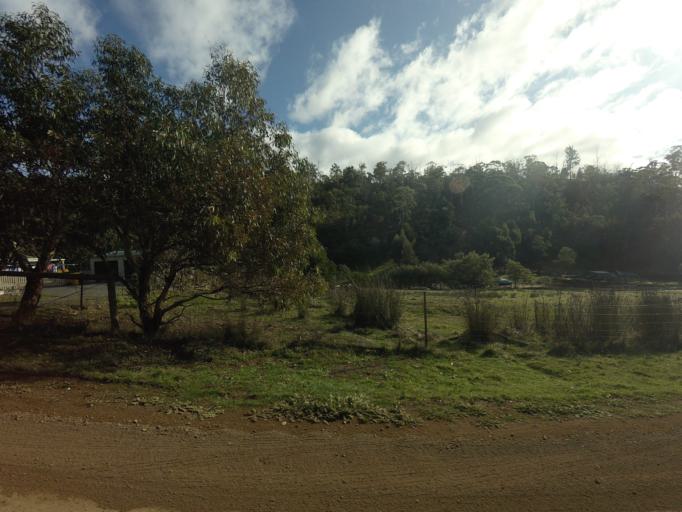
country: AU
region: Tasmania
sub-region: Derwent Valley
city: New Norfolk
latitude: -42.8077
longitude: 147.1347
